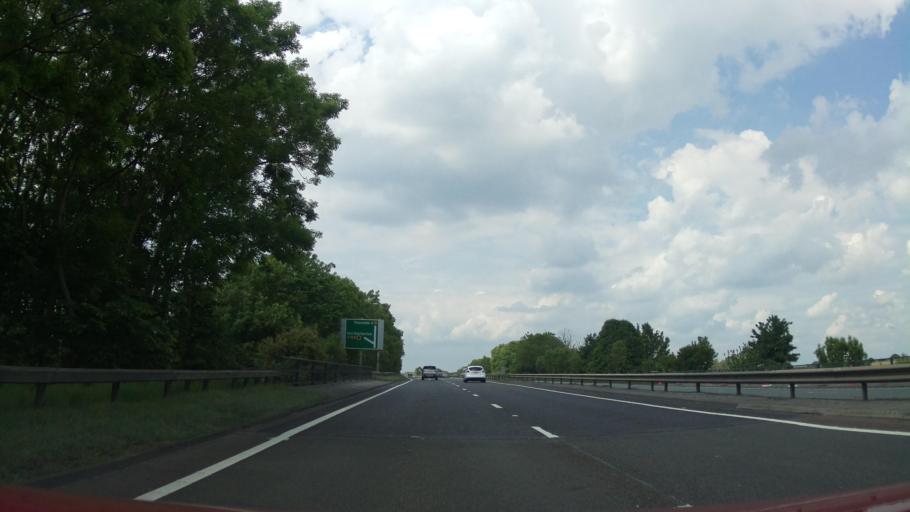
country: GB
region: England
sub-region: North Yorkshire
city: Thirsk
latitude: 54.2492
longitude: -1.3412
